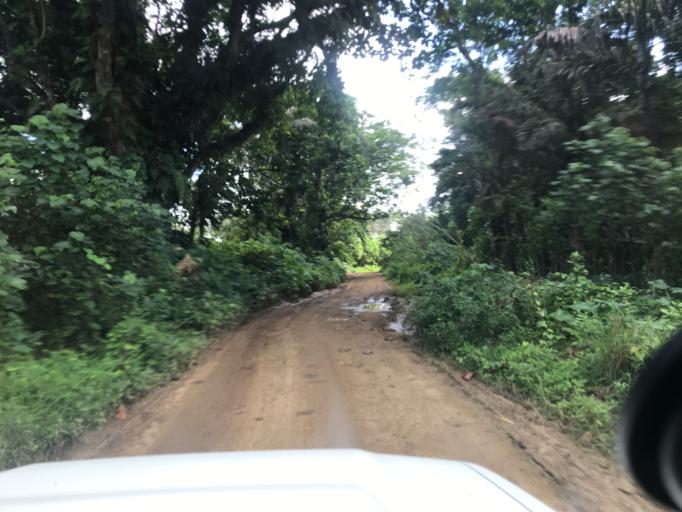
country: VU
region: Sanma
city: Luganville
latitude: -15.4872
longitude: 167.0896
